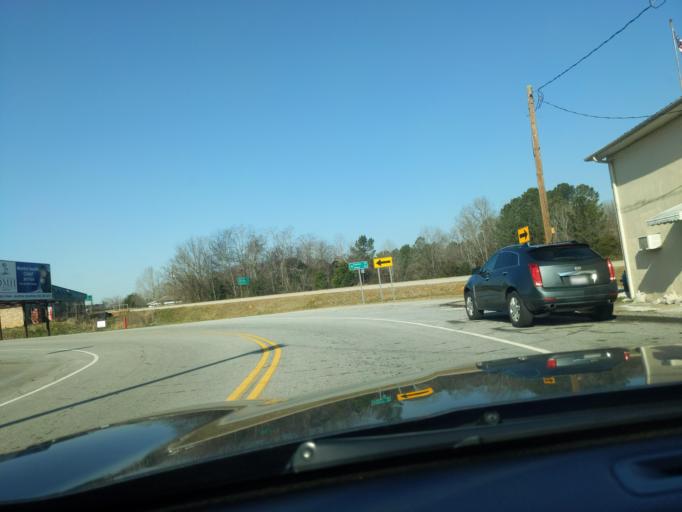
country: US
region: South Carolina
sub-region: Abbeville County
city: Calhoun Falls
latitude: 34.0923
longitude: -82.5963
